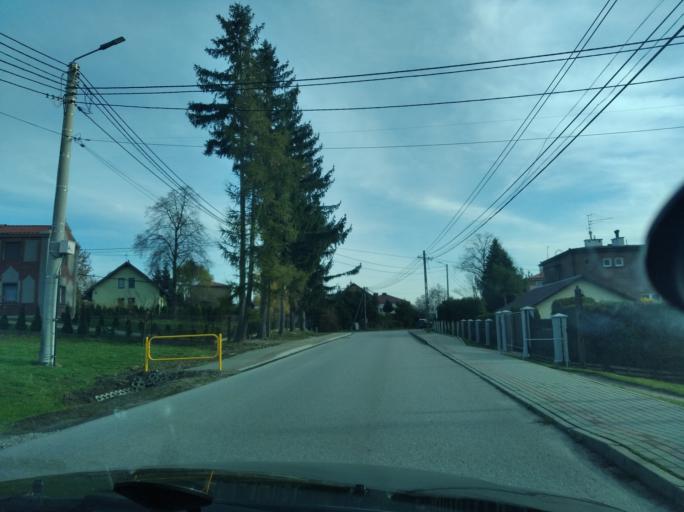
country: PL
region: Subcarpathian Voivodeship
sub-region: Powiat lancucki
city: Kraczkowa
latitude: 50.0382
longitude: 22.1658
